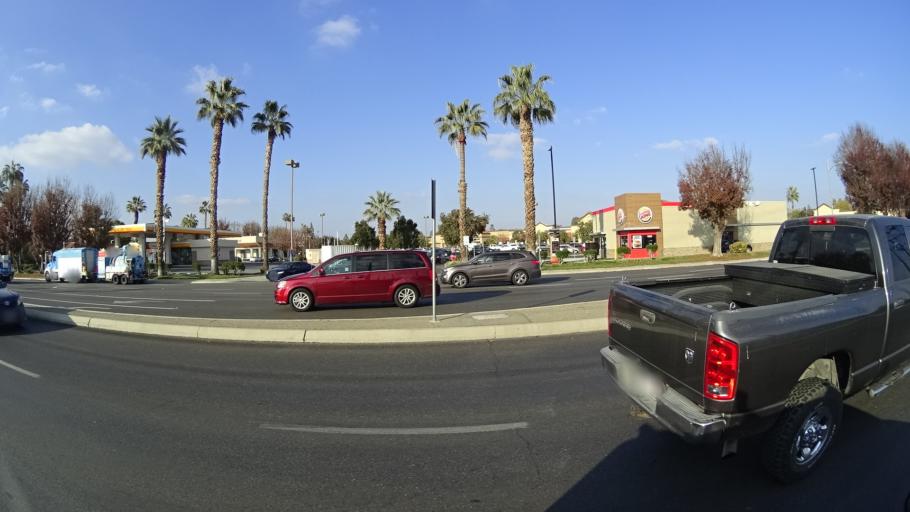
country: US
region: California
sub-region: Kern County
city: Greenacres
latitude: 35.3181
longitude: -119.0912
